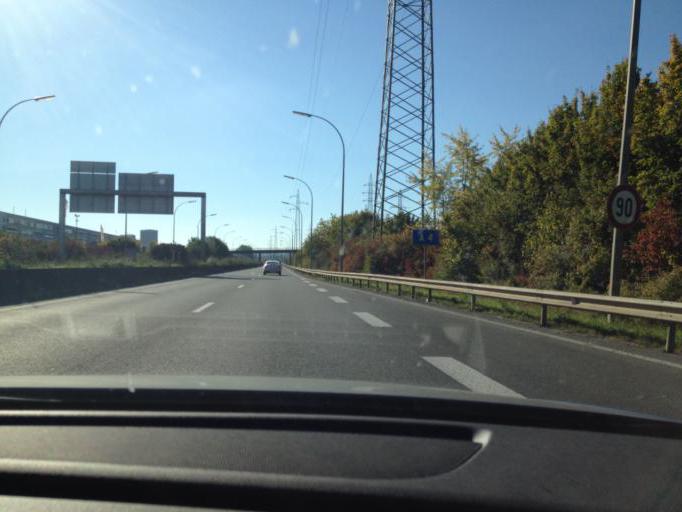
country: LU
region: Luxembourg
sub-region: Canton d'Esch-sur-Alzette
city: Esch-sur-Alzette
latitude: 49.5118
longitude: 5.9712
